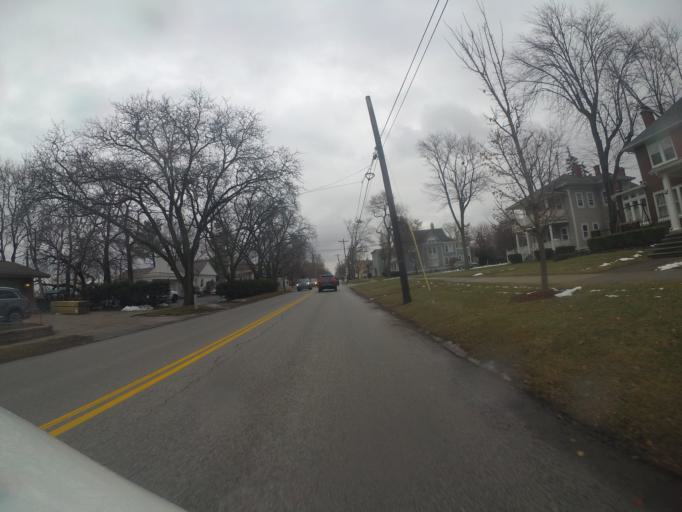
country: US
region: Ohio
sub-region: Wood County
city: Perrysburg
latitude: 41.5594
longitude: -83.6328
